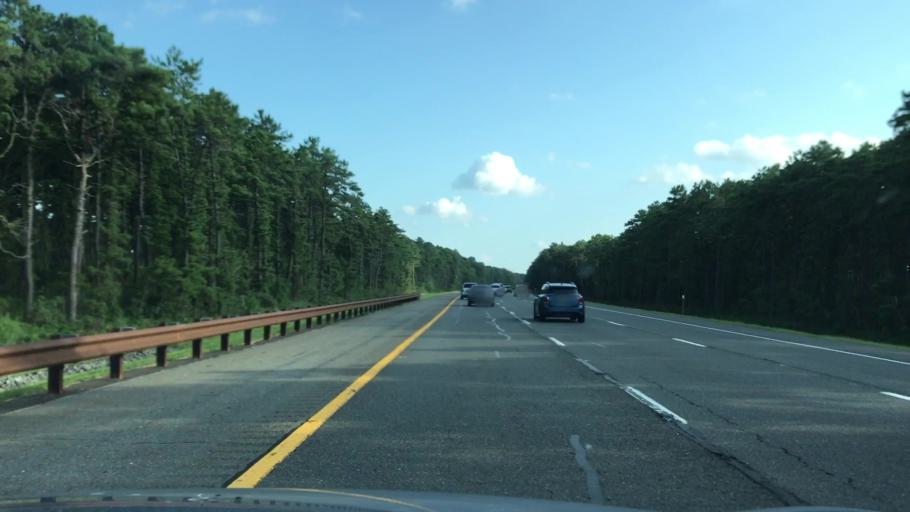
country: US
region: New Jersey
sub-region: Ocean County
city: Forked River
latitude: 39.8437
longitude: -74.2244
